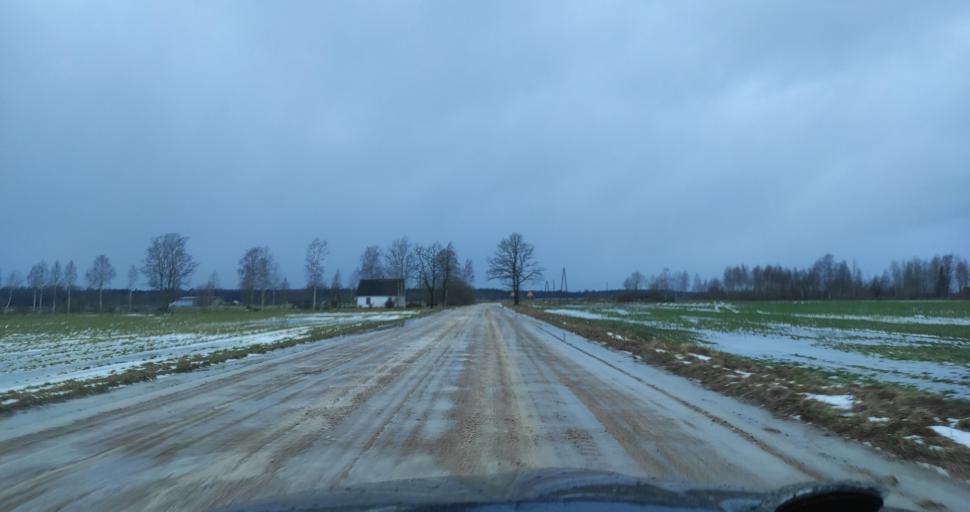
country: LV
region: Dundaga
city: Dundaga
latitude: 57.4708
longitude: 22.0202
